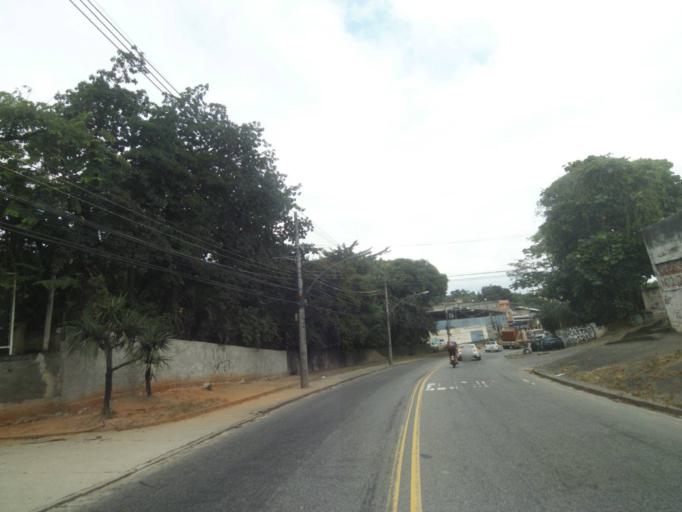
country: BR
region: Rio de Janeiro
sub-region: Sao Joao De Meriti
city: Sao Joao de Meriti
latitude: -22.9078
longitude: -43.3787
